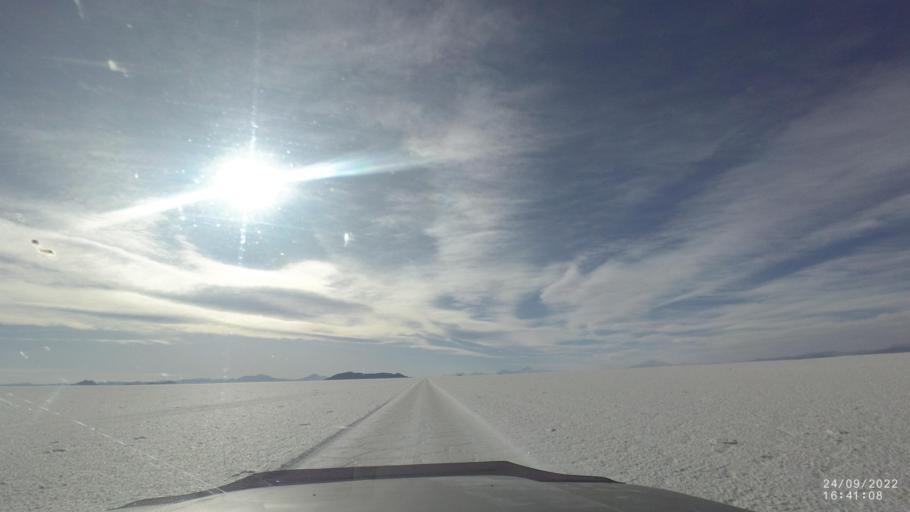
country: BO
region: Potosi
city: Colchani
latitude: -20.1880
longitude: -67.7107
